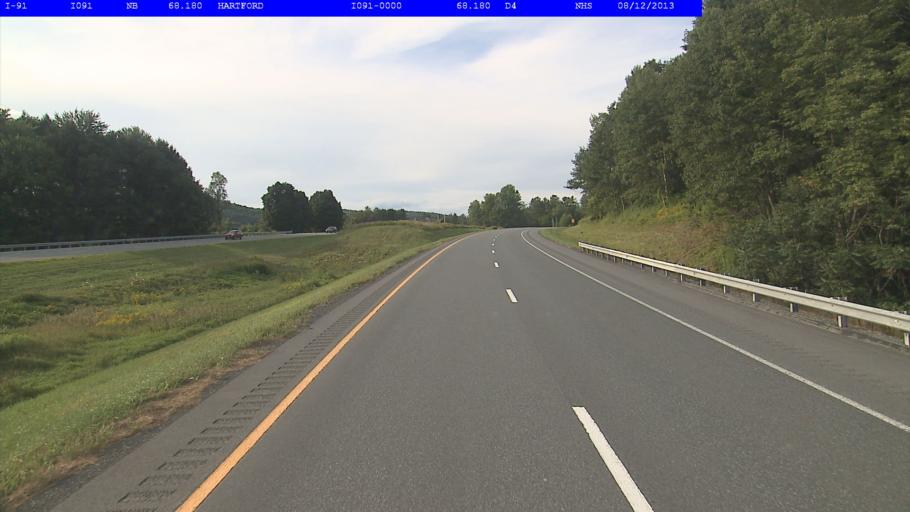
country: US
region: Vermont
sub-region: Windsor County
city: White River Junction
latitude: 43.6174
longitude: -72.3476
